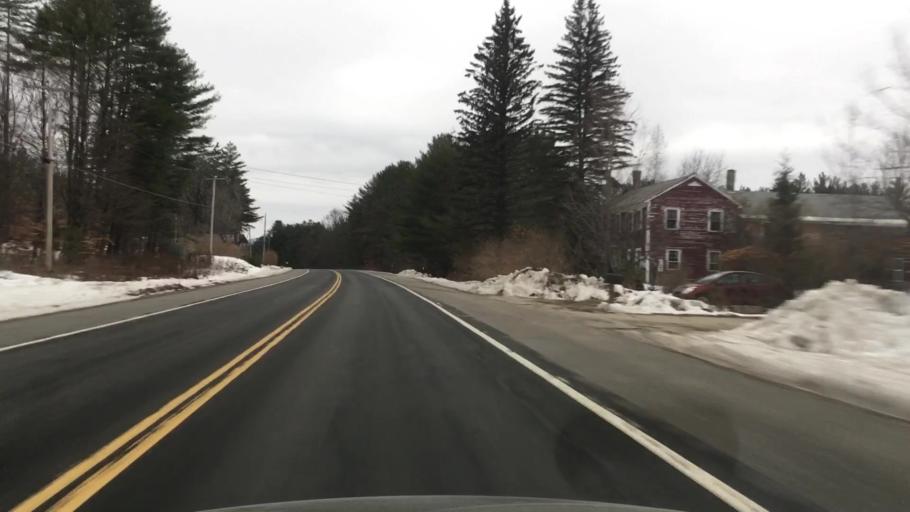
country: US
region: New Hampshire
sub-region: Merrimack County
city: Henniker
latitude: 43.2238
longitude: -71.8842
